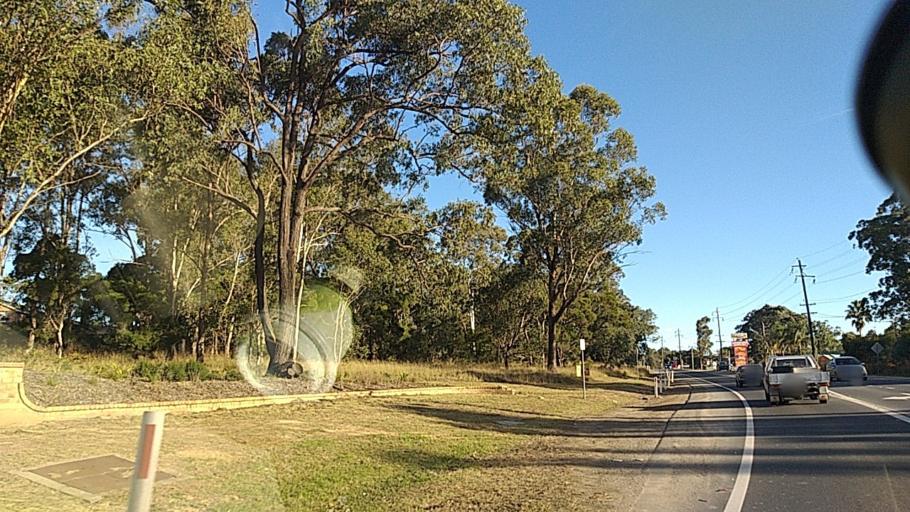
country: AU
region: New South Wales
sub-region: Hawkesbury
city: South Windsor
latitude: -33.6346
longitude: 150.7884
